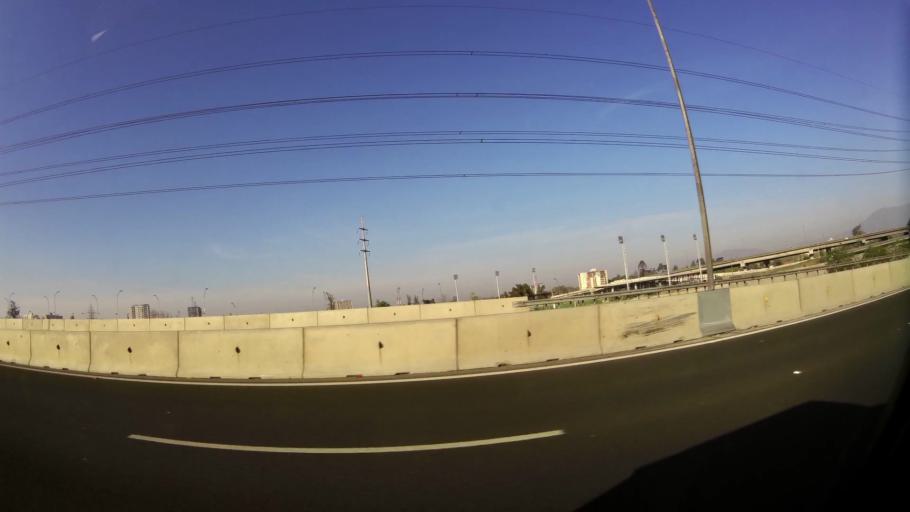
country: CL
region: Santiago Metropolitan
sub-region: Provincia de Santiago
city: Lo Prado
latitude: -33.4191
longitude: -70.6879
